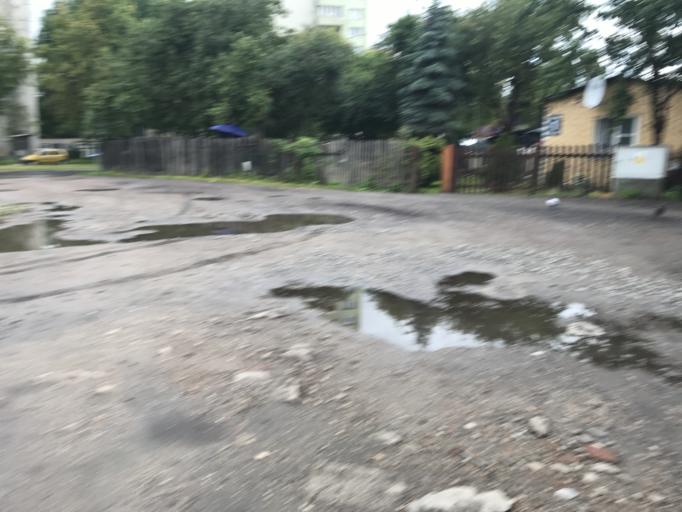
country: PL
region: Pomeranian Voivodeship
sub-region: Gdansk
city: Gdansk
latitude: 54.3509
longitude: 18.6749
